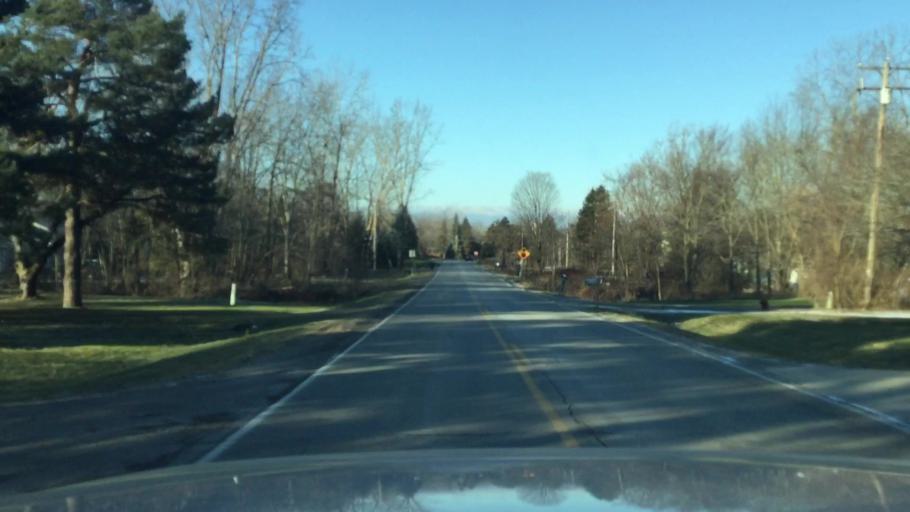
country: US
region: Michigan
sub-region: Genesee County
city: Grand Blanc
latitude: 42.9265
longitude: -83.6585
